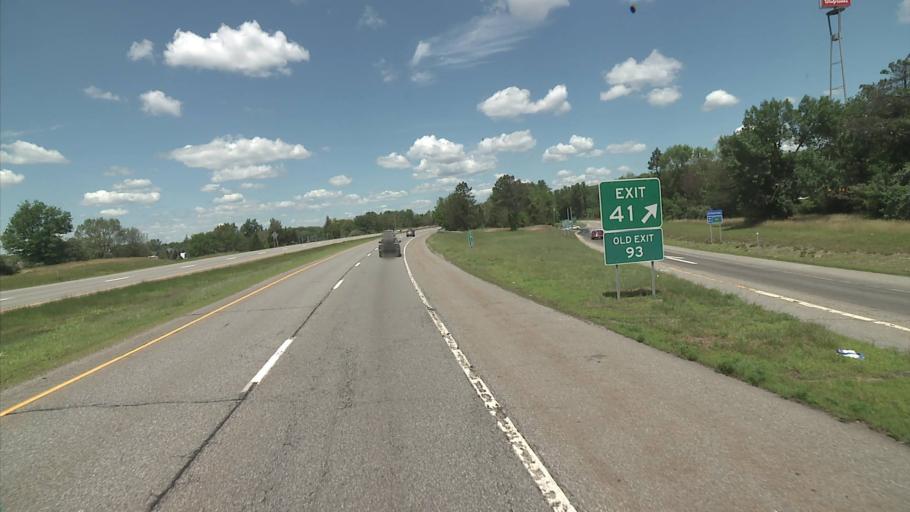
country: US
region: Connecticut
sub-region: Windham County
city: Killingly Center
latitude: 41.8405
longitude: -71.8783
